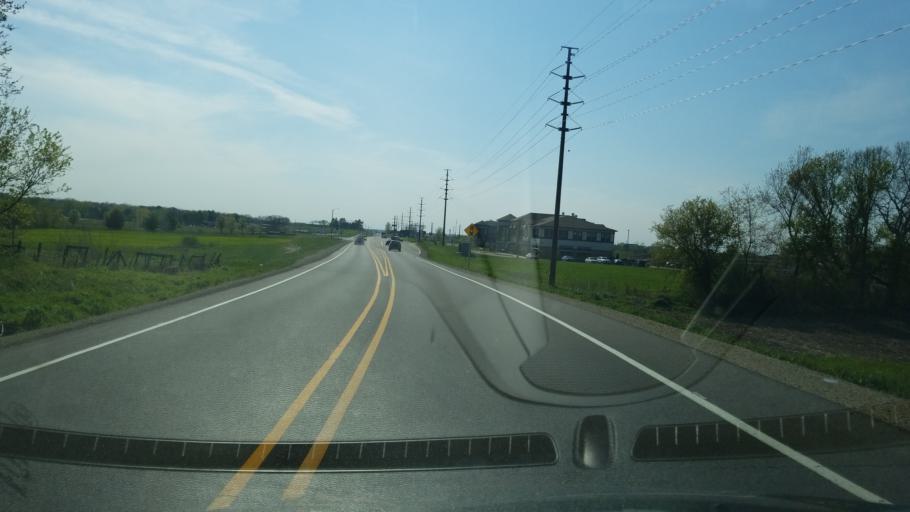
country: US
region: Wisconsin
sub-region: Dane County
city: Verona
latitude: 42.9723
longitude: -89.5036
